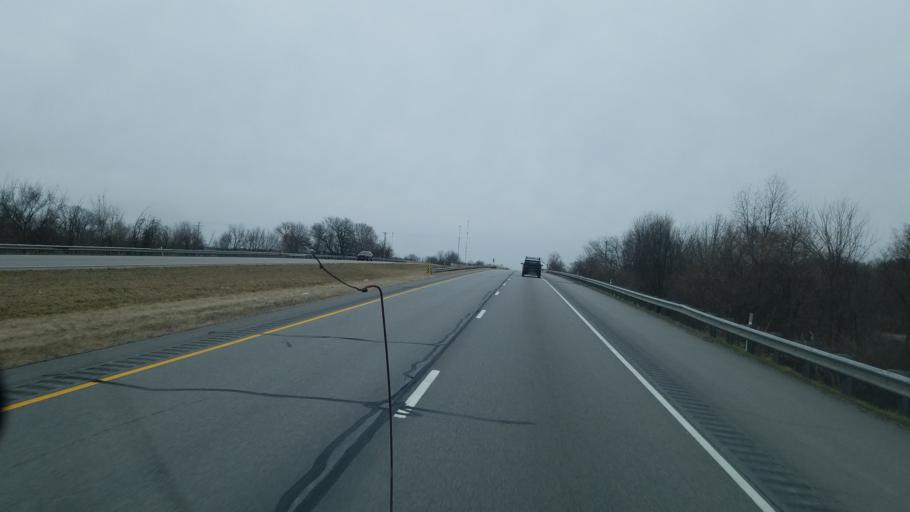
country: US
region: Indiana
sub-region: Marshall County
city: Plymouth
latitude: 41.3350
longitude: -86.2762
